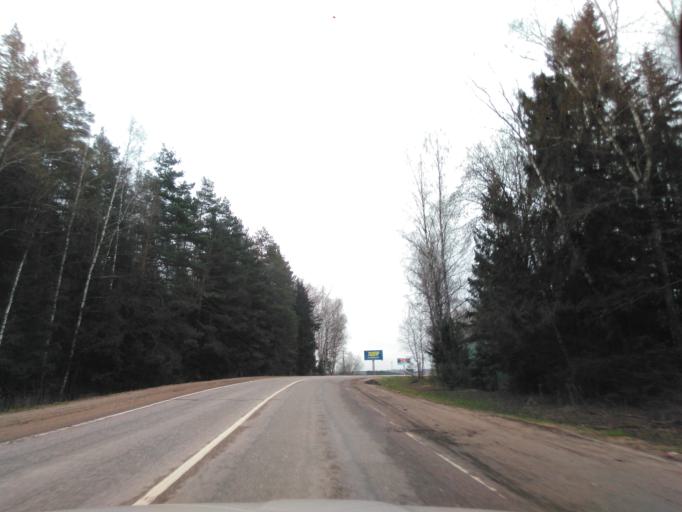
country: RU
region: Moskovskaya
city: Rozhdestveno
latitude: 55.8318
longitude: 37.0270
